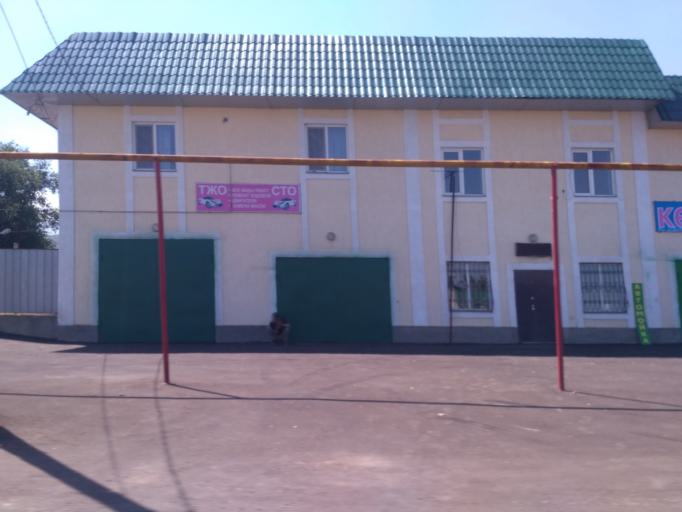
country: KZ
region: Almaty Oblysy
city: Burunday
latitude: 43.1665
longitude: 76.5906
